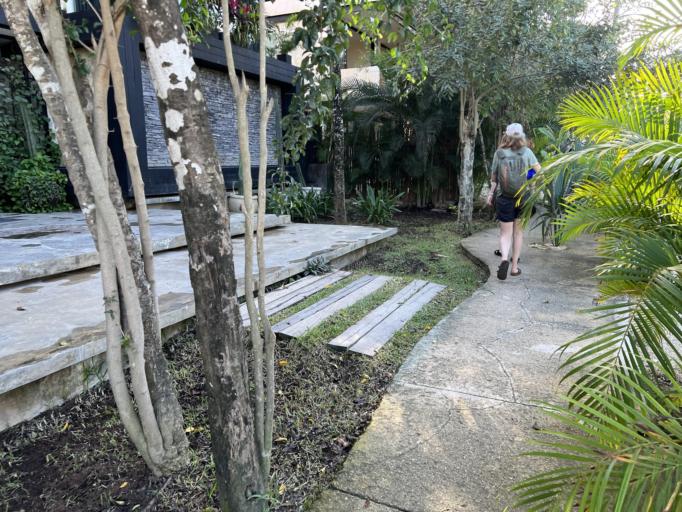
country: MX
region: Quintana Roo
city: Tulum
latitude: 20.2044
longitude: -87.4584
